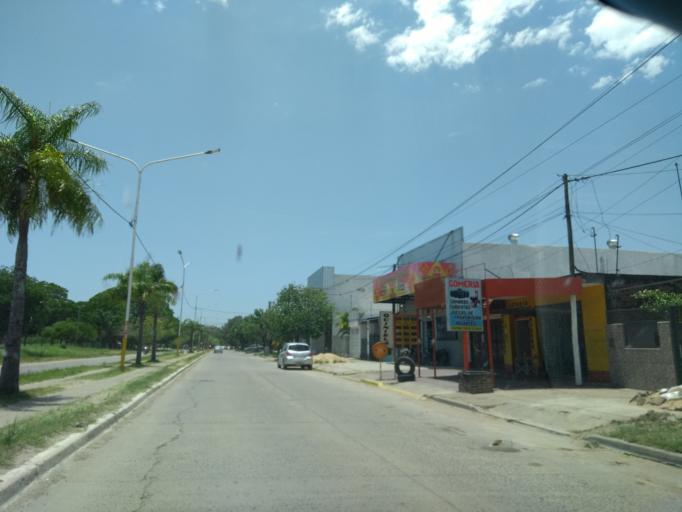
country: AR
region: Chaco
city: Barranqueras
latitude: -27.4852
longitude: -58.9530
